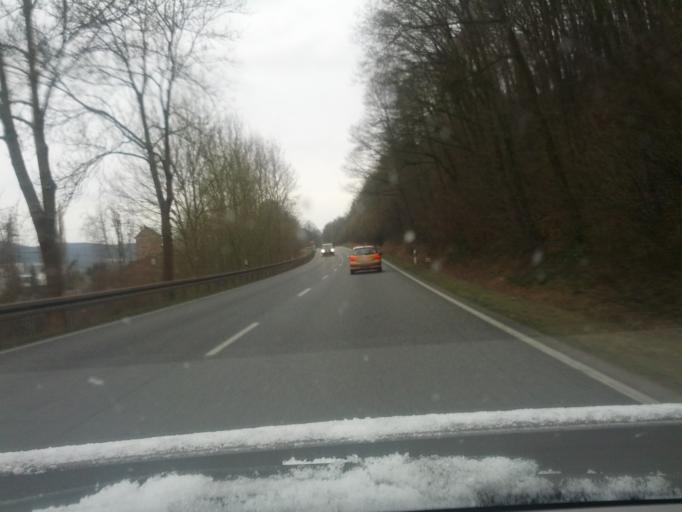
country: DE
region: Hesse
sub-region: Regierungsbezirk Kassel
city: Sontra
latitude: 51.1210
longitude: 9.9756
